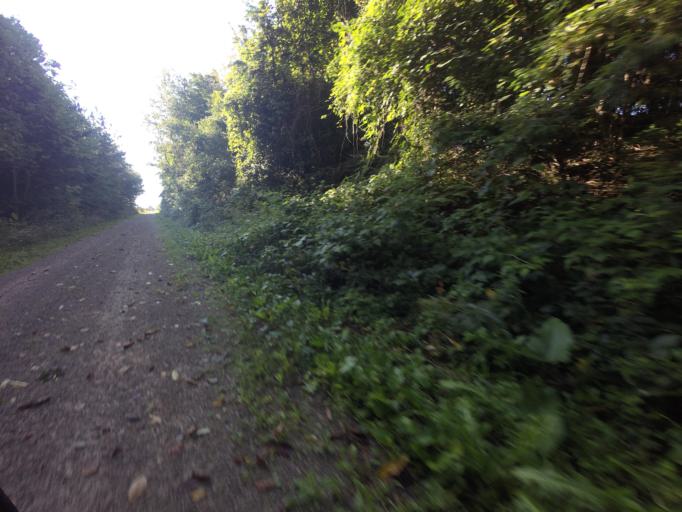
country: CA
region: Ontario
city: Goderich
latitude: 43.7572
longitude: -81.5159
